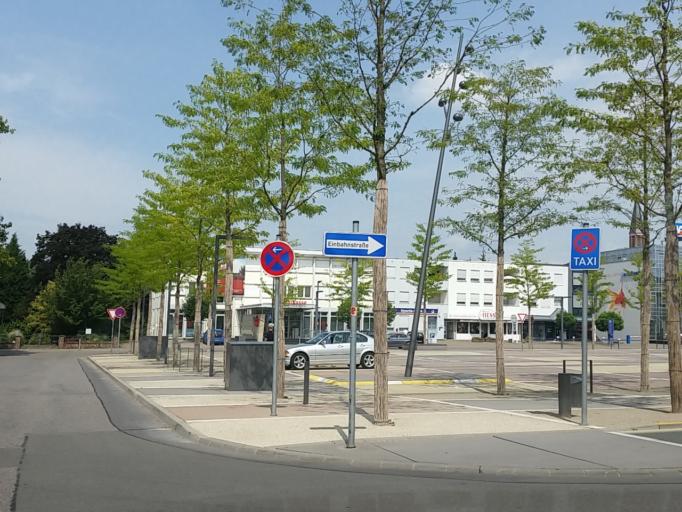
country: DE
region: Saarland
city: Lebach
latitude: 49.4087
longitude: 6.9082
